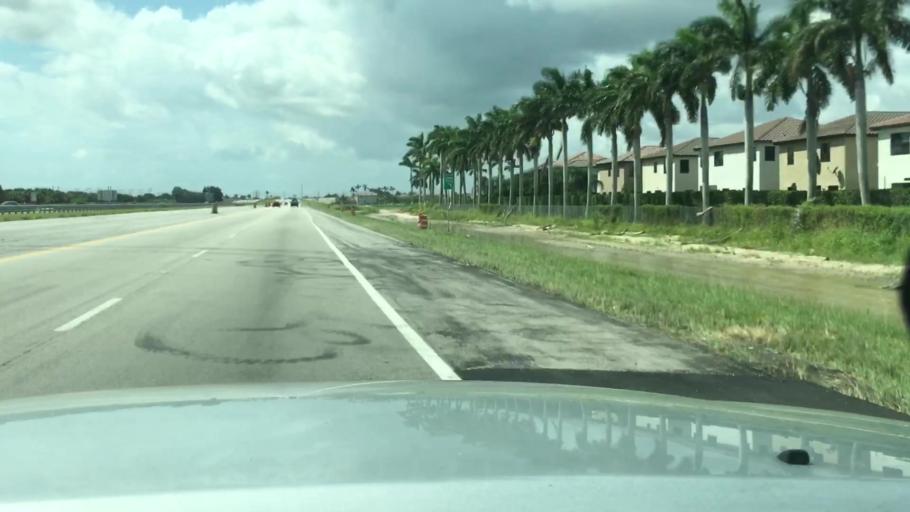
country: US
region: Florida
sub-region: Miami-Dade County
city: Princeton
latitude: 25.5312
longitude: -80.3804
